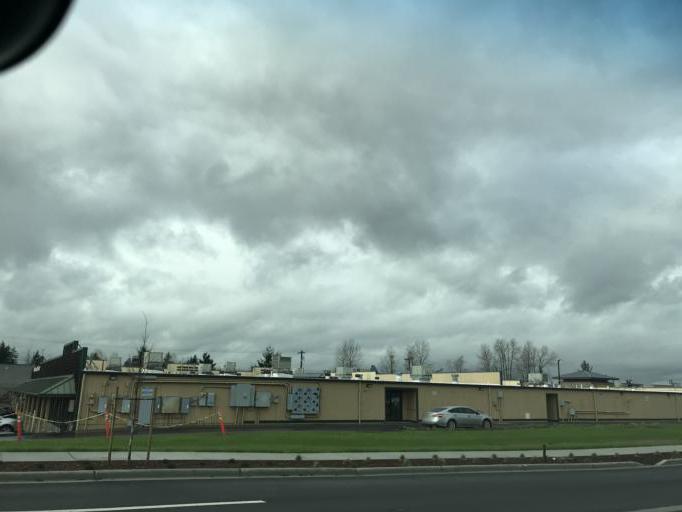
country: US
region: Washington
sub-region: Snohomish County
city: West Lake Stevens
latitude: 48.0000
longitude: -122.1042
